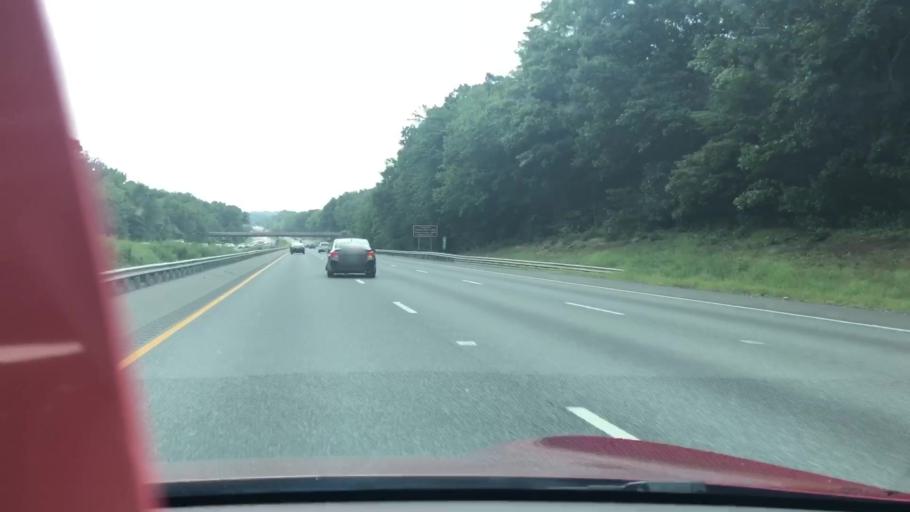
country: US
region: Maryland
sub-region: Harford County
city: Aberdeen
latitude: 39.5589
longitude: -76.1520
